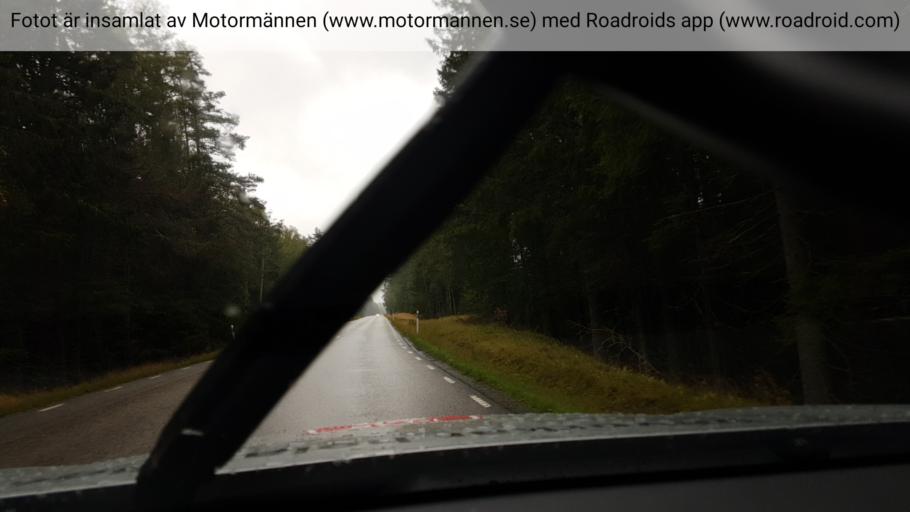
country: SE
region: Vaestra Goetaland
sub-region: Bengtsfors Kommun
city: Dals Langed
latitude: 58.8373
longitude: 12.1510
